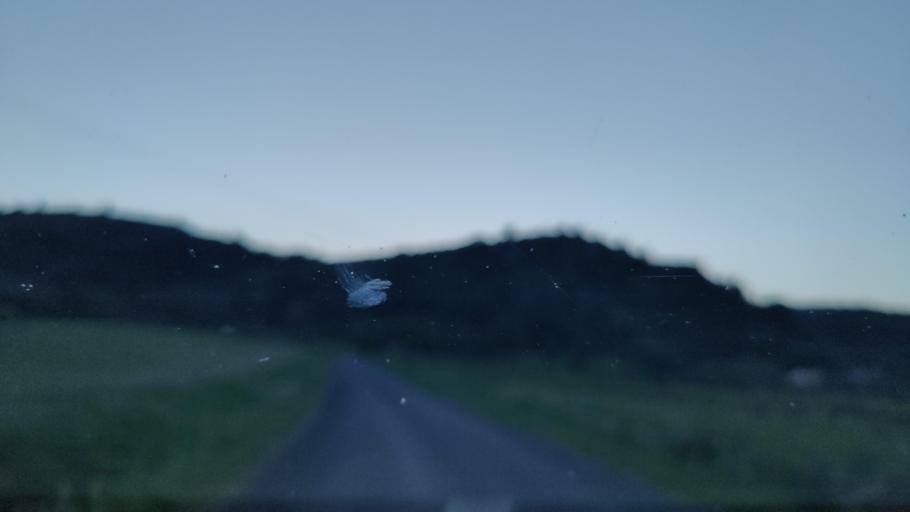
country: FR
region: Languedoc-Roussillon
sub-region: Departement des Pyrenees-Orientales
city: Baixas
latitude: 42.8511
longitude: 2.7743
